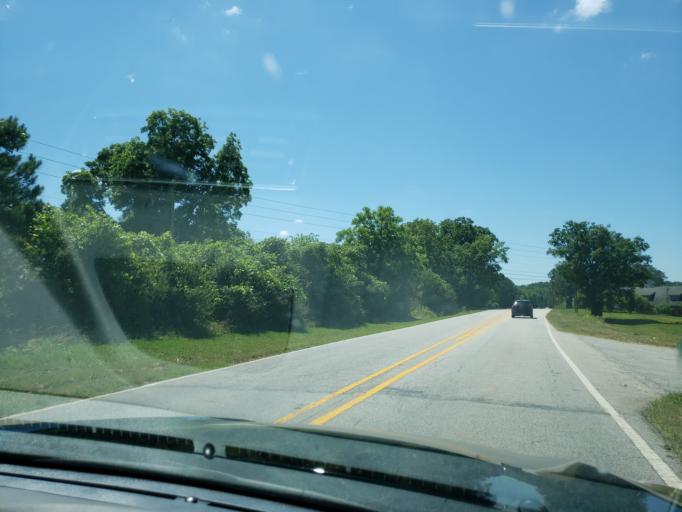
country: US
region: Alabama
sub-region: Lee County
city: Auburn
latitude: 32.6548
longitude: -85.4860
